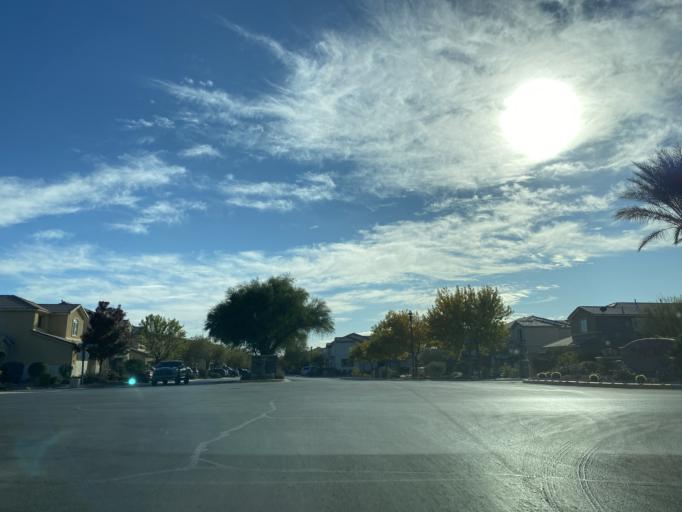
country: US
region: Nevada
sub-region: Clark County
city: North Las Vegas
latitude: 36.3128
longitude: -115.2429
